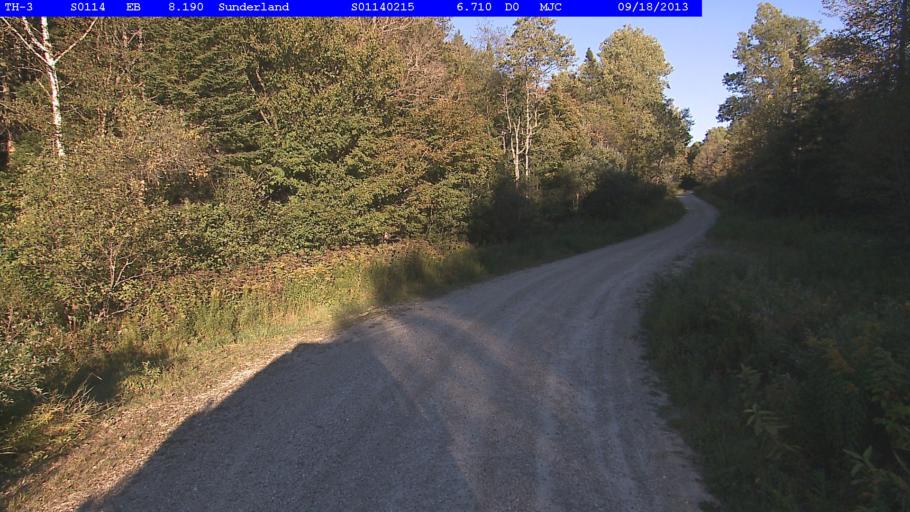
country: US
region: Vermont
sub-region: Bennington County
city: Arlington
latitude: 43.0532
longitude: -73.0546
